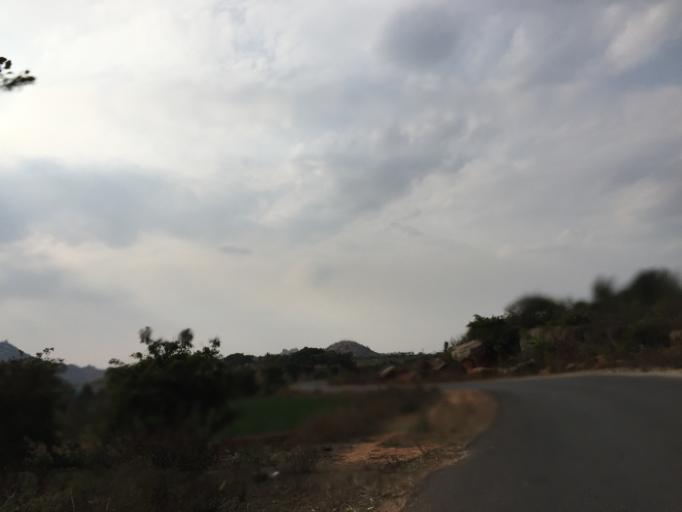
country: IN
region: Karnataka
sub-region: Chikkaballapur
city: Chik Ballapur
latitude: 13.5501
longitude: 77.7601
